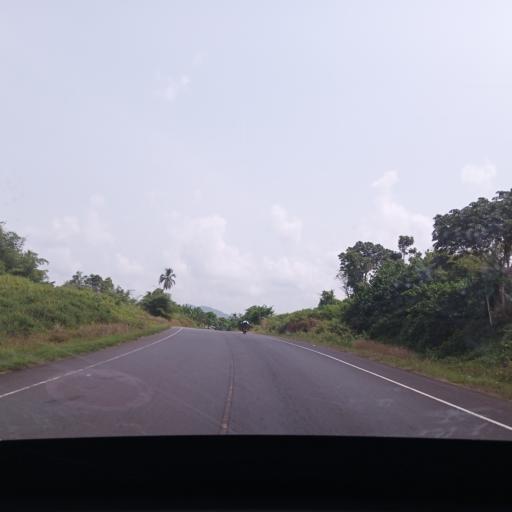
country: LR
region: Margibi
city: Kakata
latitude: 6.2527
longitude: -10.3043
